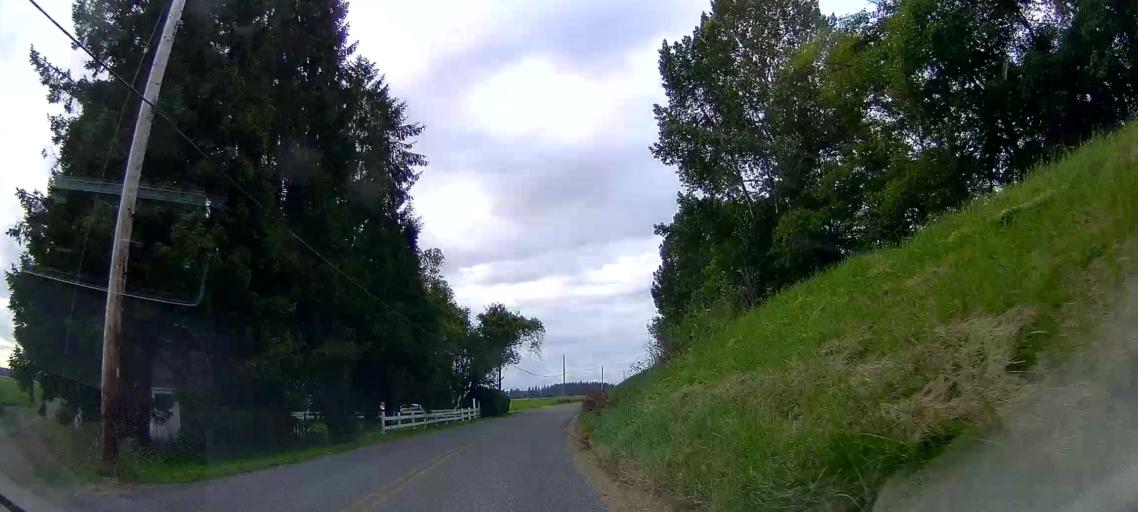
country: US
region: Washington
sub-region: Skagit County
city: Mount Vernon
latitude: 48.3505
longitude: -122.3618
